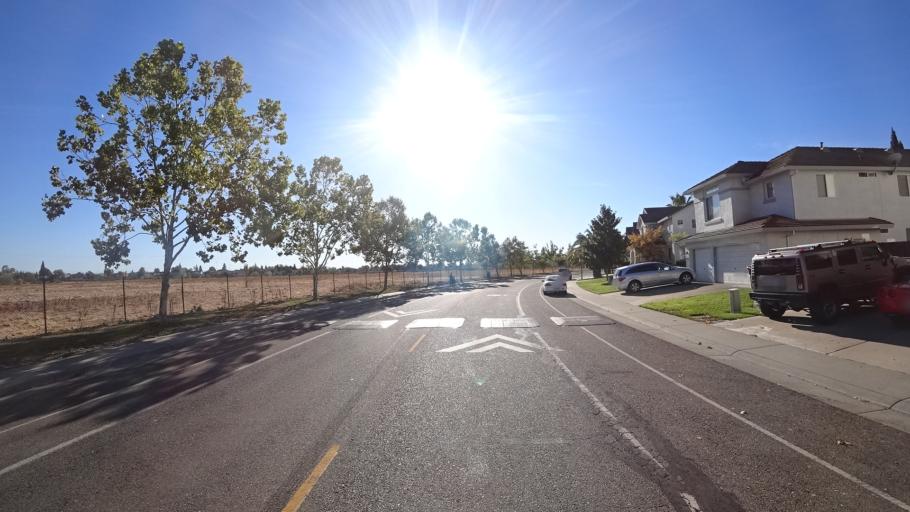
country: US
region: California
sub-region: Sacramento County
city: Vineyard
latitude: 38.4478
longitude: -121.3824
